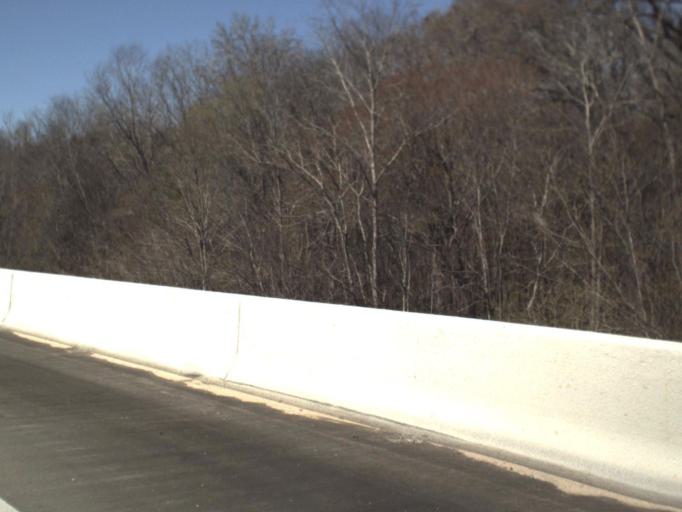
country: US
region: Florida
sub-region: Gadsden County
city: Chattahoochee
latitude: 30.6990
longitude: -84.8639
